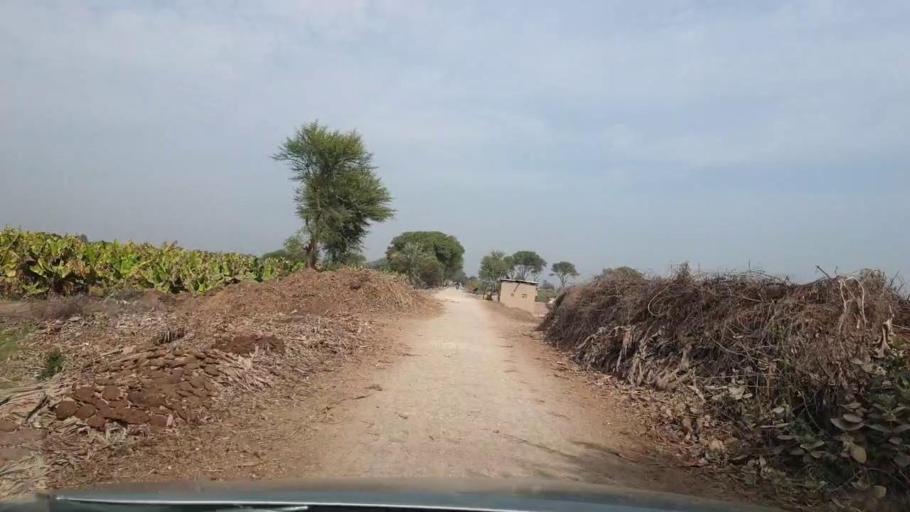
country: PK
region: Sindh
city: Tando Jam
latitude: 25.5223
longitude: 68.5570
